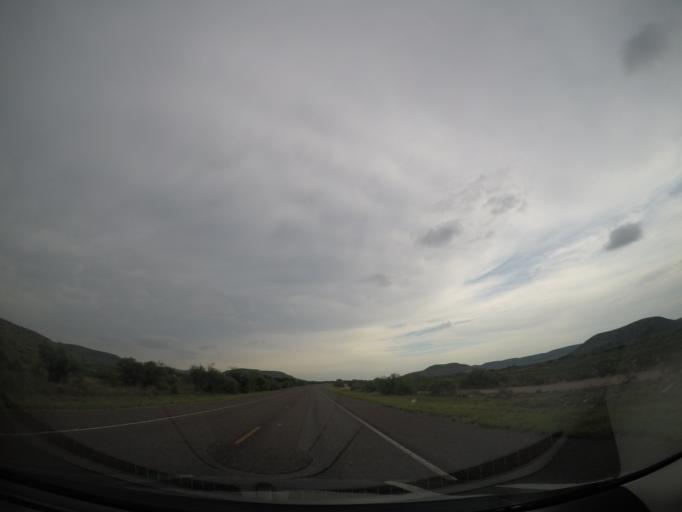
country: US
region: Texas
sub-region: Terrell County
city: Sanderson
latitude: 30.1719
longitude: -102.6969
